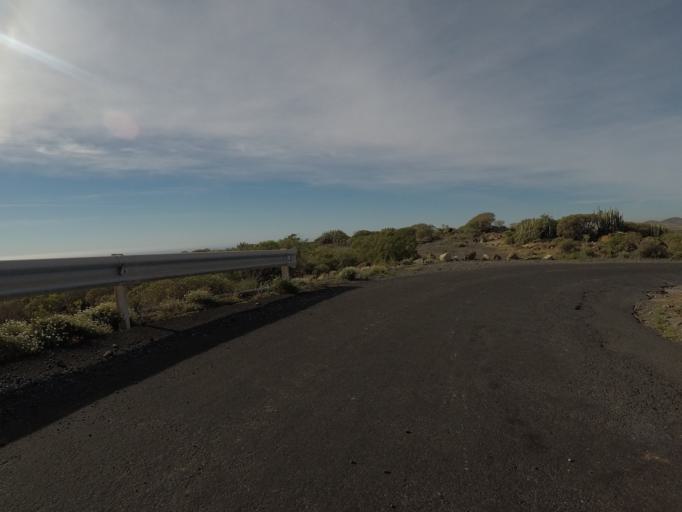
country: ES
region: Canary Islands
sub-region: Provincia de Santa Cruz de Tenerife
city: Lomo de Arico
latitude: 28.1391
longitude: -16.4807
